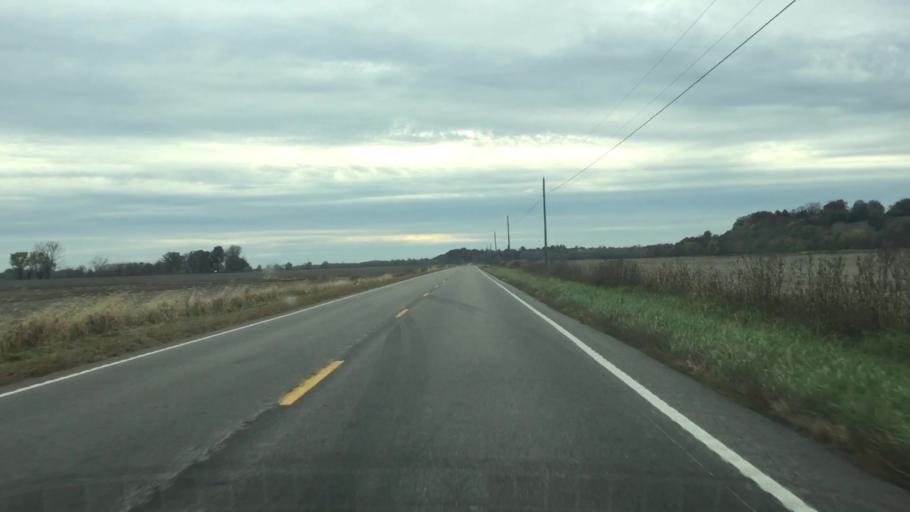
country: US
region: Missouri
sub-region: Callaway County
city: Fulton
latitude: 38.7055
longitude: -91.7994
